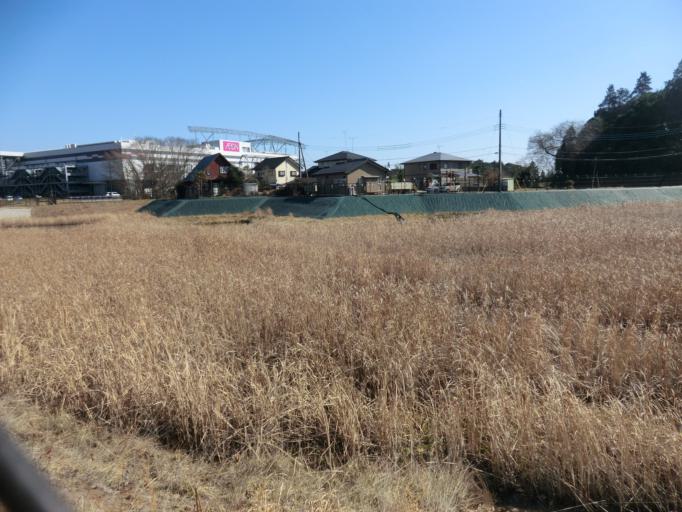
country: JP
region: Ibaraki
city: Naka
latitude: 36.0337
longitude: 140.1292
